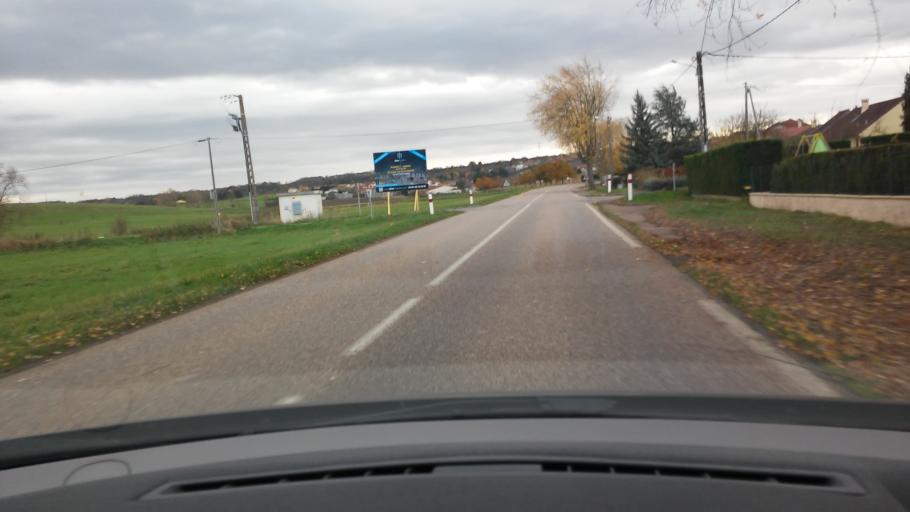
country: FR
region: Lorraine
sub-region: Departement de la Moselle
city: Saint-Julien-les-Metz
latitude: 49.1614
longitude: 6.2293
